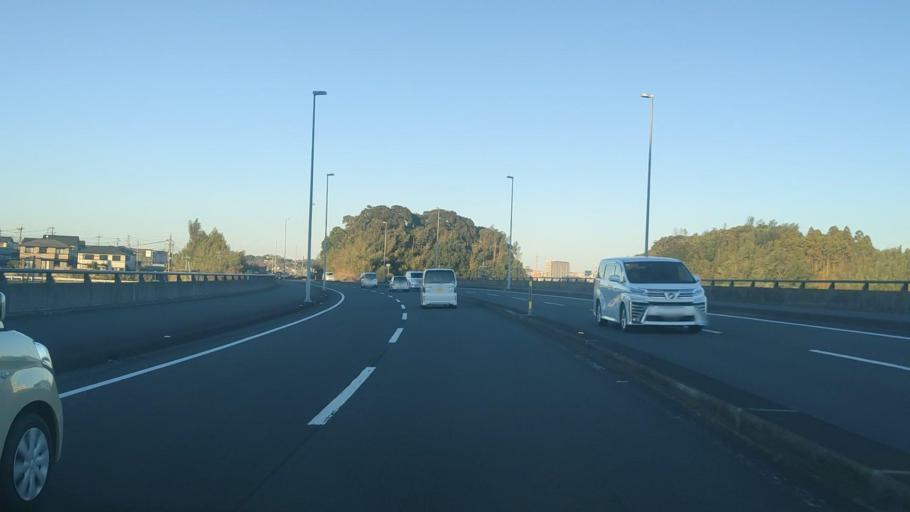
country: JP
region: Miyazaki
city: Miyazaki-shi
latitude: 31.8869
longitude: 131.4020
